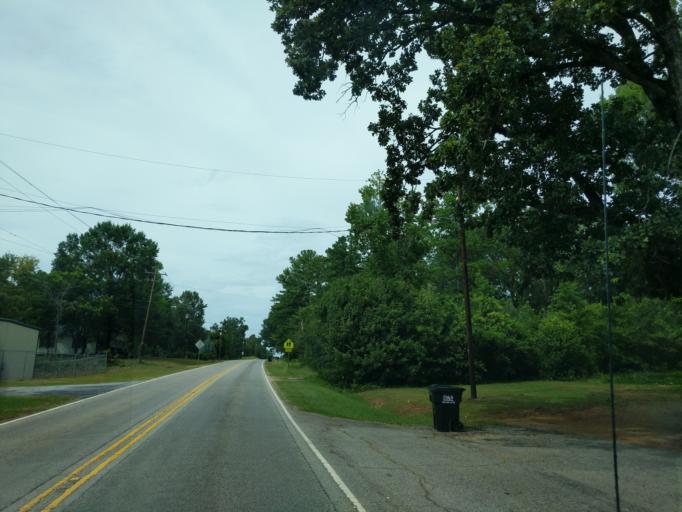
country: US
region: South Carolina
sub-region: Abbeville County
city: Calhoun Falls
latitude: 34.0962
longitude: -82.5986
